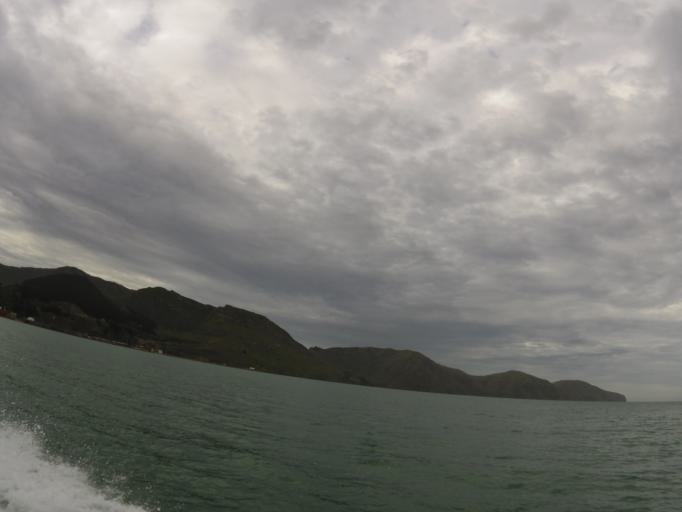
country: NZ
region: Canterbury
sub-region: Christchurch City
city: Christchurch
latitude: -43.6218
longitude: 172.7340
